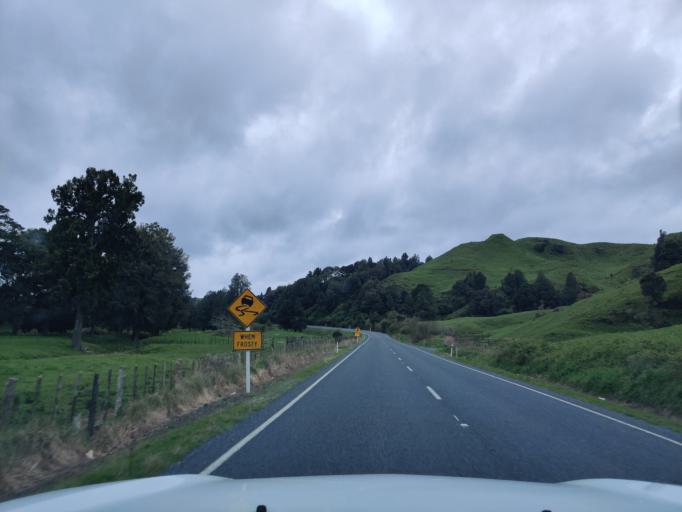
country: NZ
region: Waikato
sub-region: Otorohanga District
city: Otorohanga
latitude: -38.5444
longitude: 175.1839
